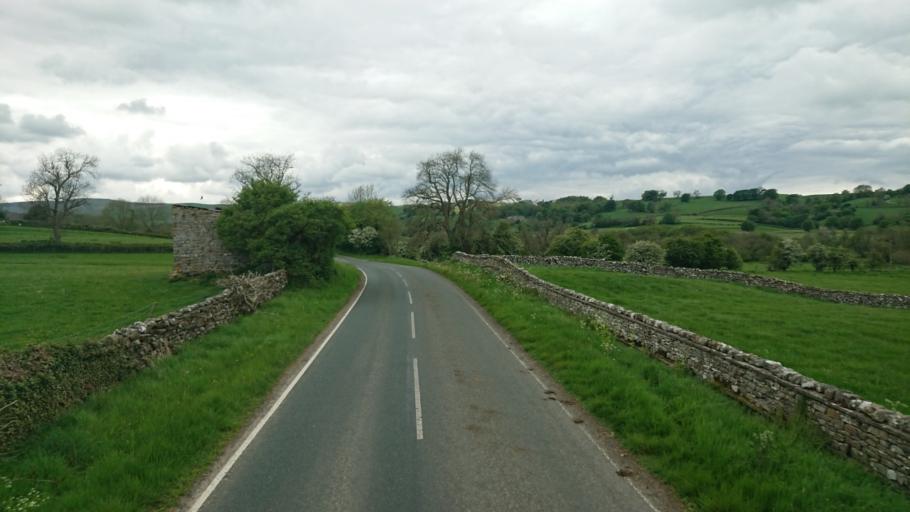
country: GB
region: England
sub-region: North Yorkshire
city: Leyburn
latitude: 54.2763
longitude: -1.9808
